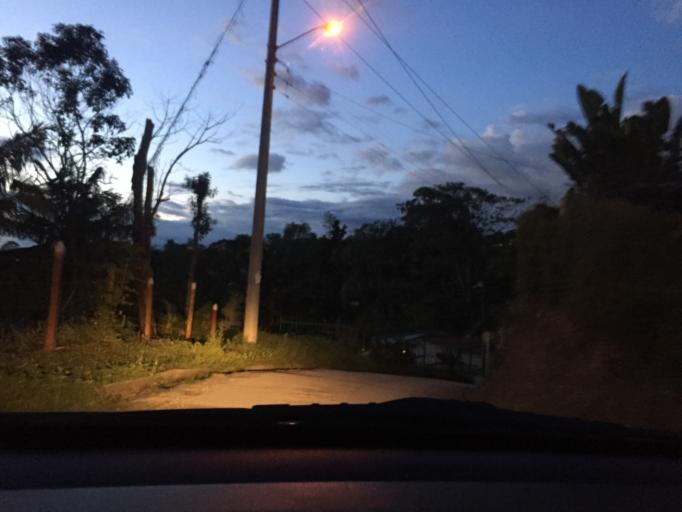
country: CO
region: Cundinamarca
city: Zipacon
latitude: 4.7247
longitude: -74.4177
